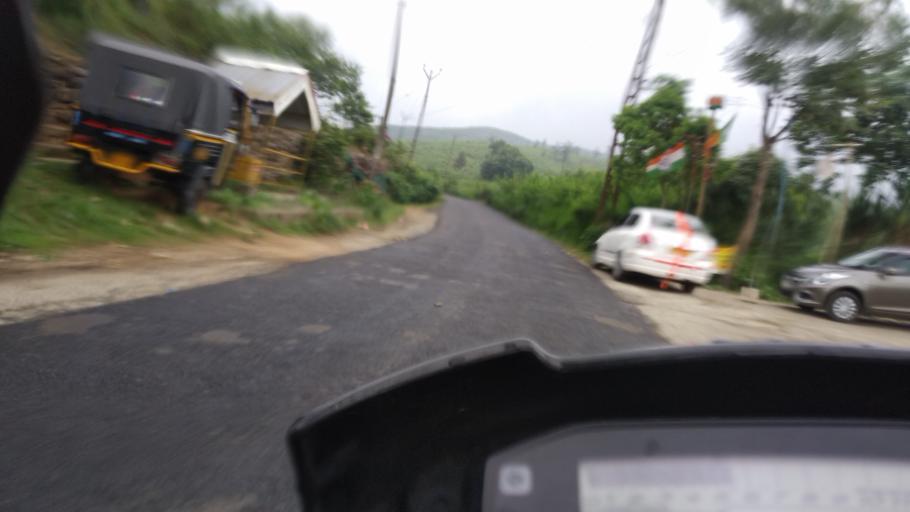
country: IN
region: Kerala
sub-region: Kottayam
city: Erattupetta
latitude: 9.6378
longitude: 76.9330
